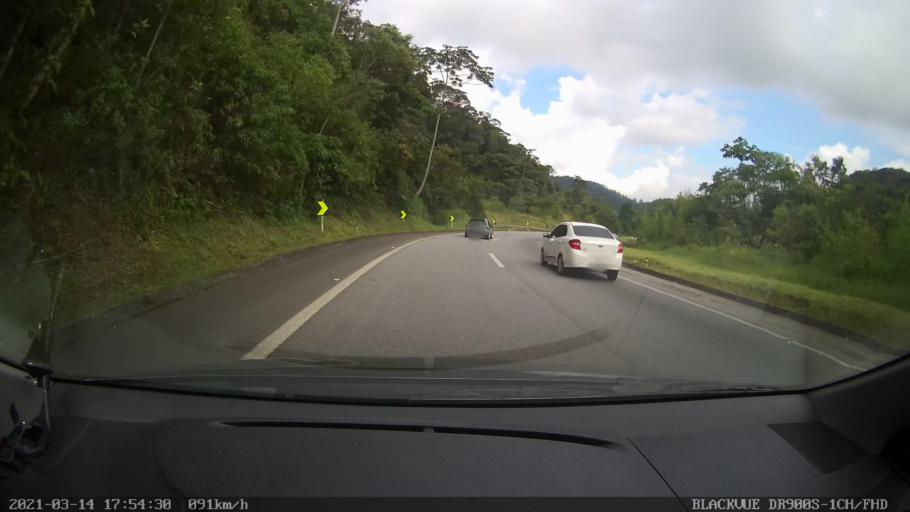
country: BR
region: Rio de Janeiro
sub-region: Petropolis
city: Petropolis
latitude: -22.4872
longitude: -43.2250
